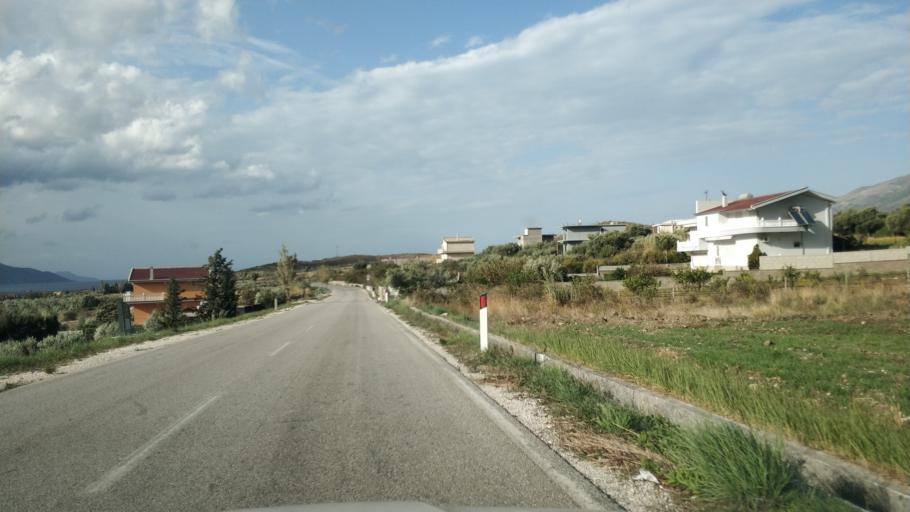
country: AL
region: Vlore
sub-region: Rrethi i Vlores
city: Orikum
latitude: 40.3079
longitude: 19.4818
